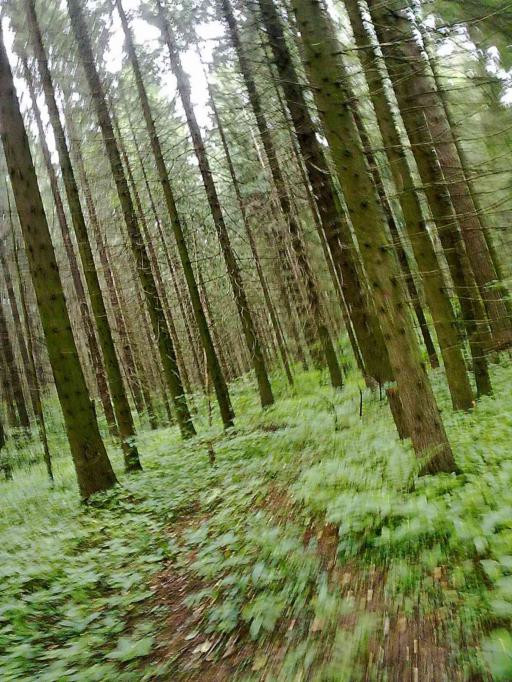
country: RU
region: Moskovskaya
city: Filimonki
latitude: 55.5533
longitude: 37.3786
